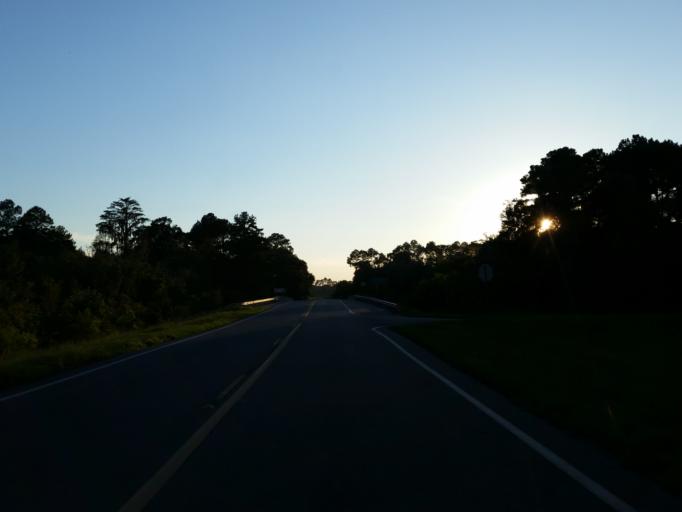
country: US
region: Georgia
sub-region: Berrien County
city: Nashville
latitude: 31.1862
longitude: -83.1782
